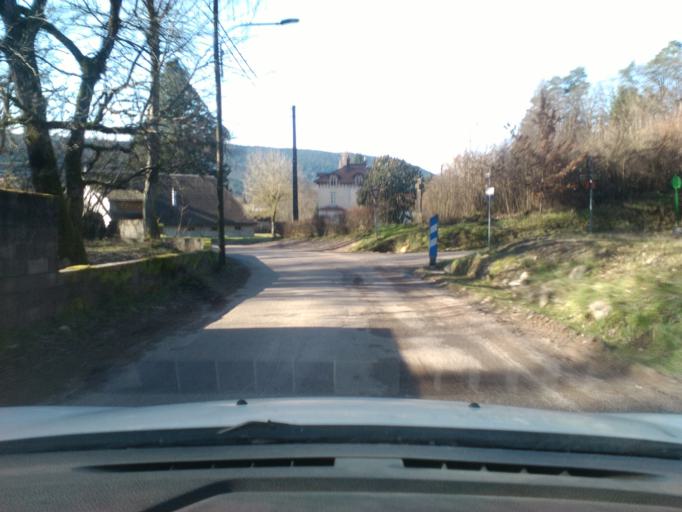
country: FR
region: Lorraine
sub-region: Departement des Vosges
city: Vecoux
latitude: 47.9796
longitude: 6.6407
